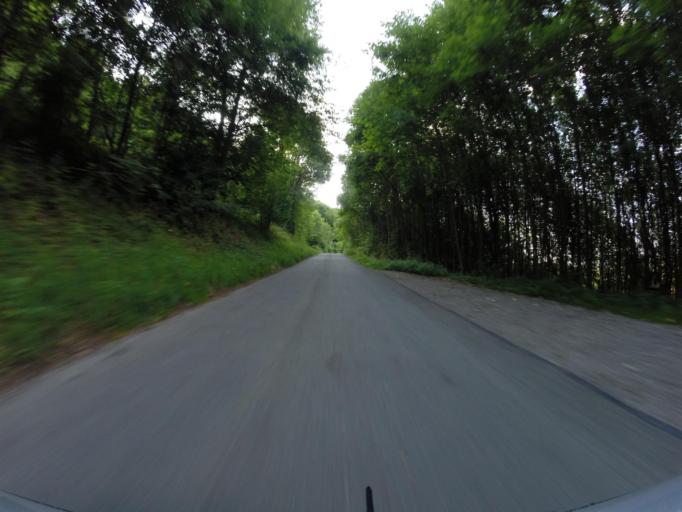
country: DE
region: Thuringia
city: Wichmar
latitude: 51.0307
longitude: 11.6829
